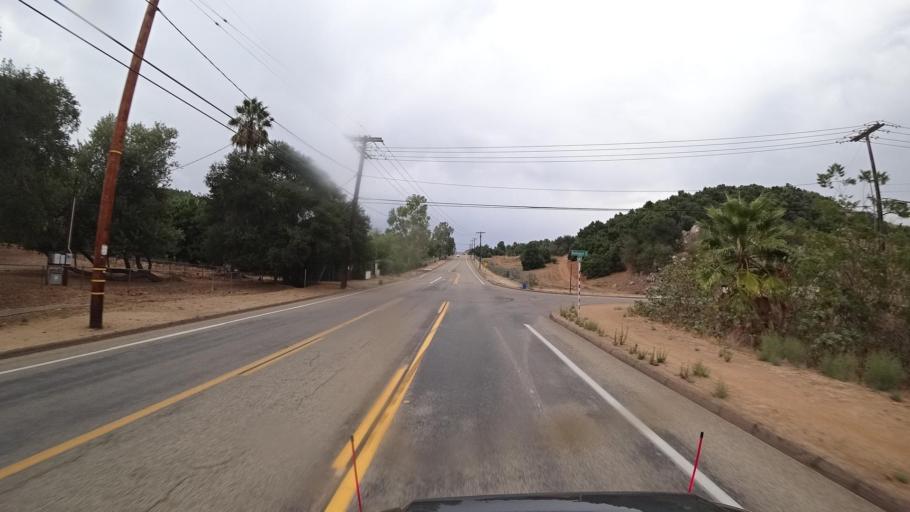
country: US
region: California
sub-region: San Diego County
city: San Pasqual
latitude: 33.1141
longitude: -117.0174
